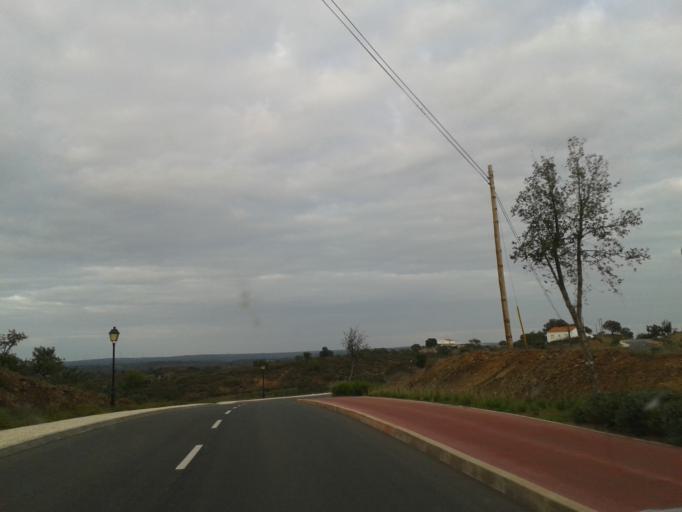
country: PT
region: Faro
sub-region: Castro Marim
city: Castro Marim
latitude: 37.2410
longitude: -7.4624
